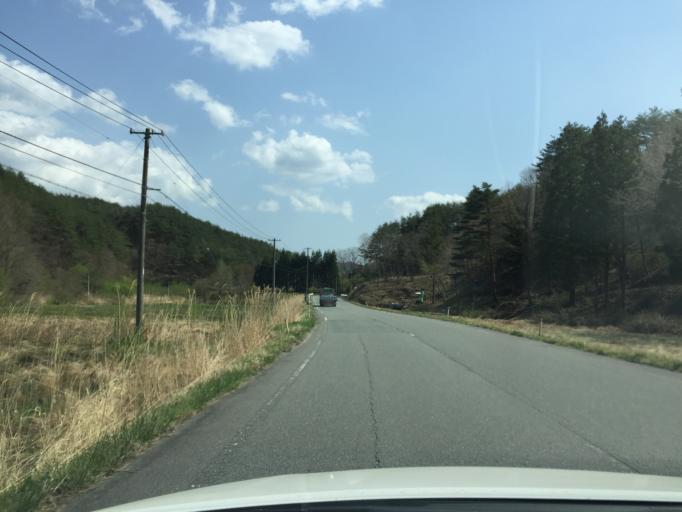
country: JP
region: Fukushima
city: Namie
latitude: 37.3687
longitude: 140.8073
